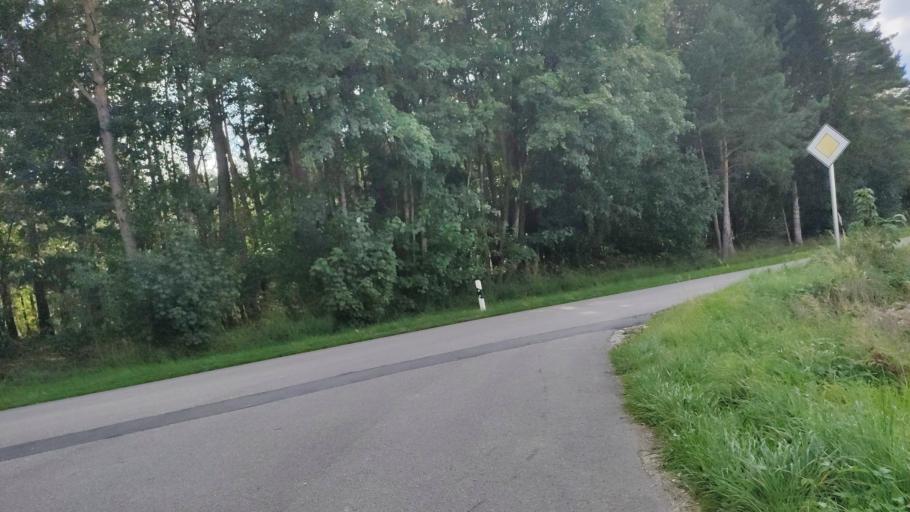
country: DE
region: Bavaria
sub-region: Swabia
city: Oberottmarshausen
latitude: 48.2201
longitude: 10.8768
